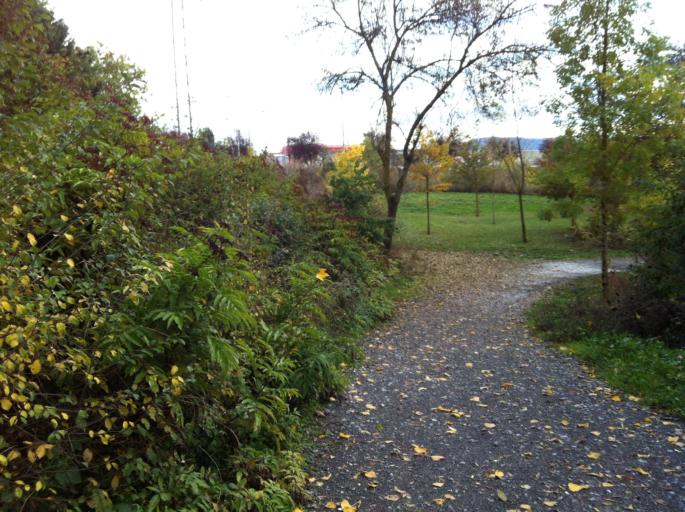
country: ES
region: Basque Country
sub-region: Provincia de Alava
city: Gasteiz / Vitoria
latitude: 42.8652
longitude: -2.7133
